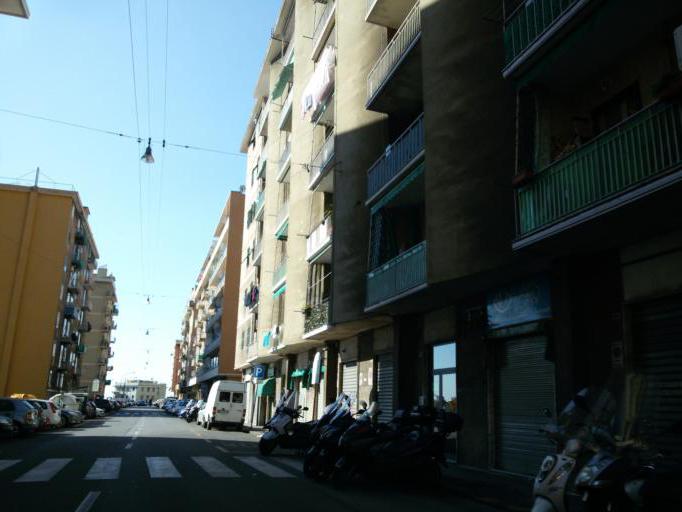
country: IT
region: Liguria
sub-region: Provincia di Genova
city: Genoa
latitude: 44.4229
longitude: 8.9165
